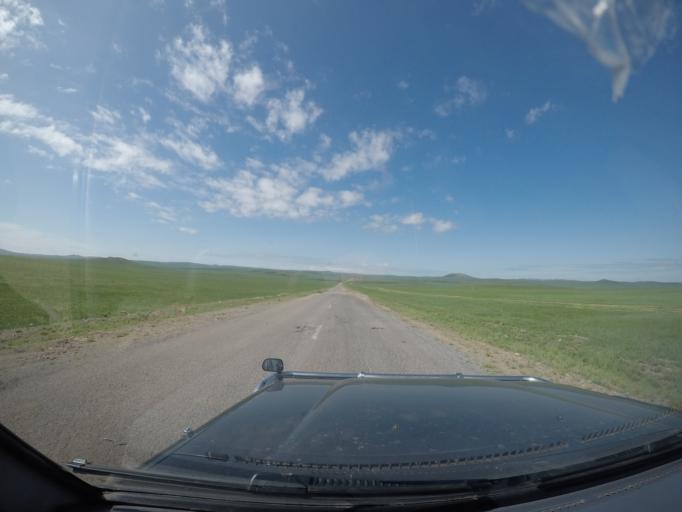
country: MN
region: Suhbaatar
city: Hanhohiy
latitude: 47.3767
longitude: 111.7929
